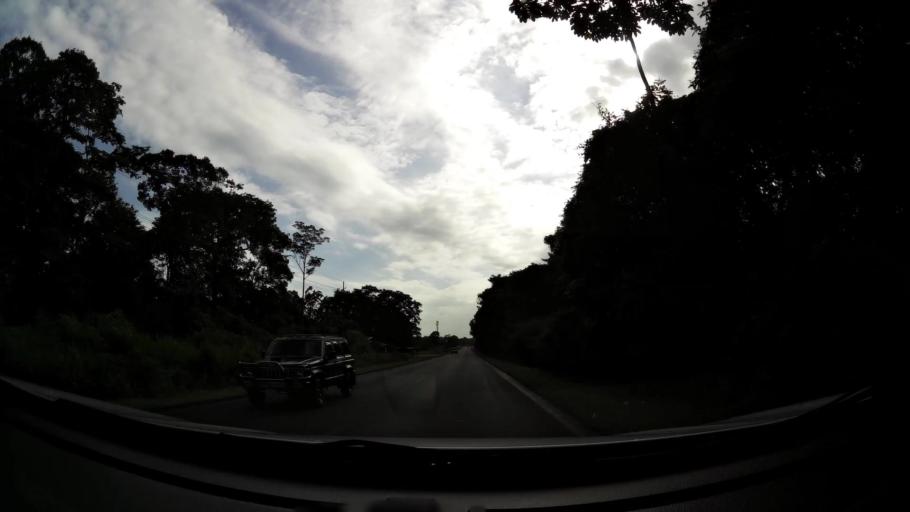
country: CR
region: Limon
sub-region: Canton de Guacimo
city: Guacimo
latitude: 10.1968
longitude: -83.6525
